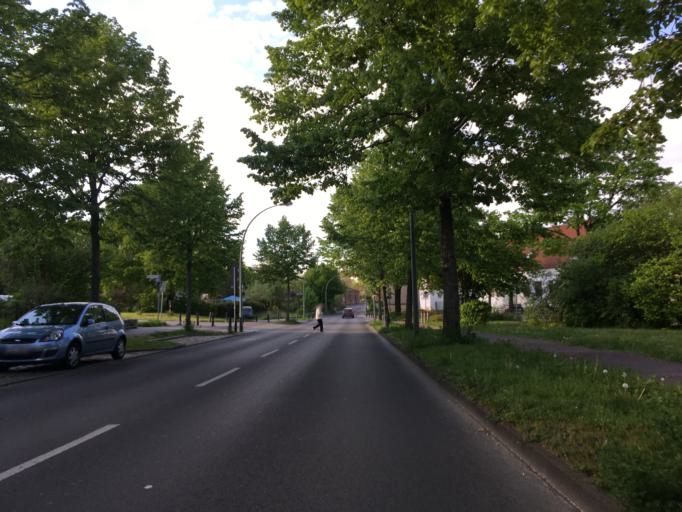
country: DE
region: Berlin
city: Wartenberg
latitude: 52.5717
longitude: 13.5207
